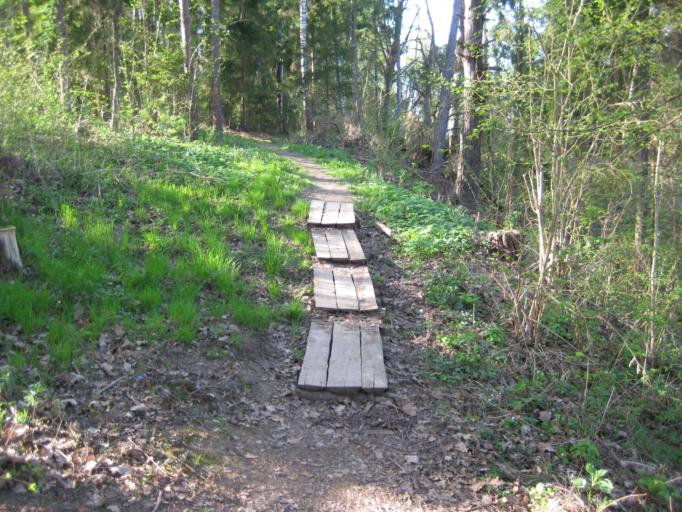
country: LT
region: Kauno apskritis
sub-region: Kauno rajonas
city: Karmelava
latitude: 54.8114
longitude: 24.1856
